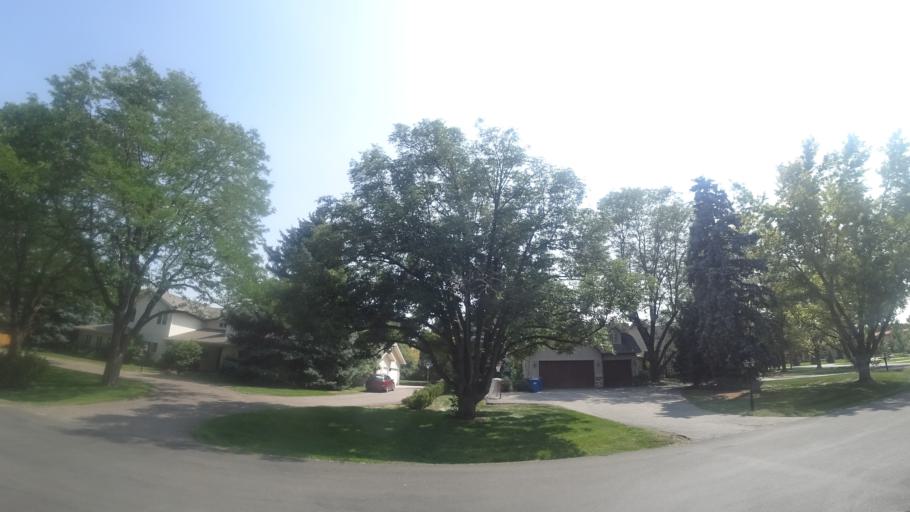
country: US
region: Colorado
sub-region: Arapahoe County
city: Cherry Hills Village
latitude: 39.6269
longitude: -104.9768
